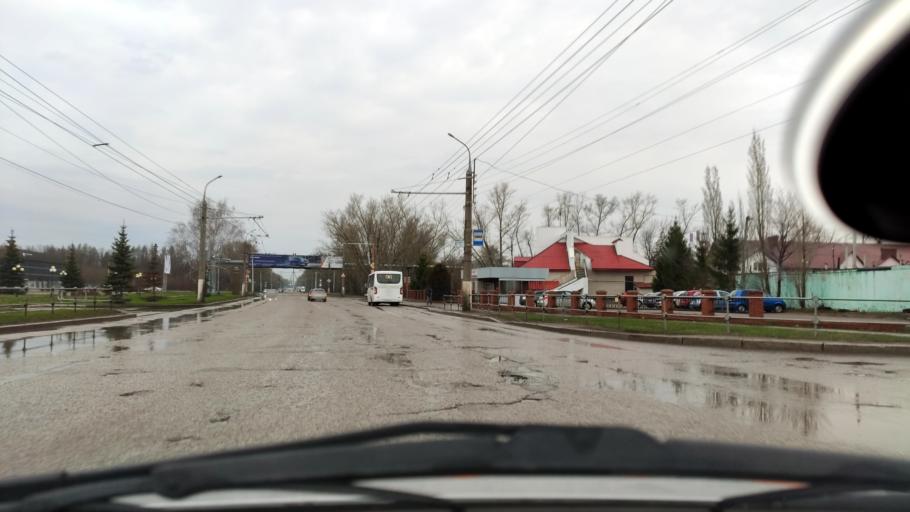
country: RU
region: Bashkortostan
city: Sterlitamak
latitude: 53.6542
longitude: 55.9484
